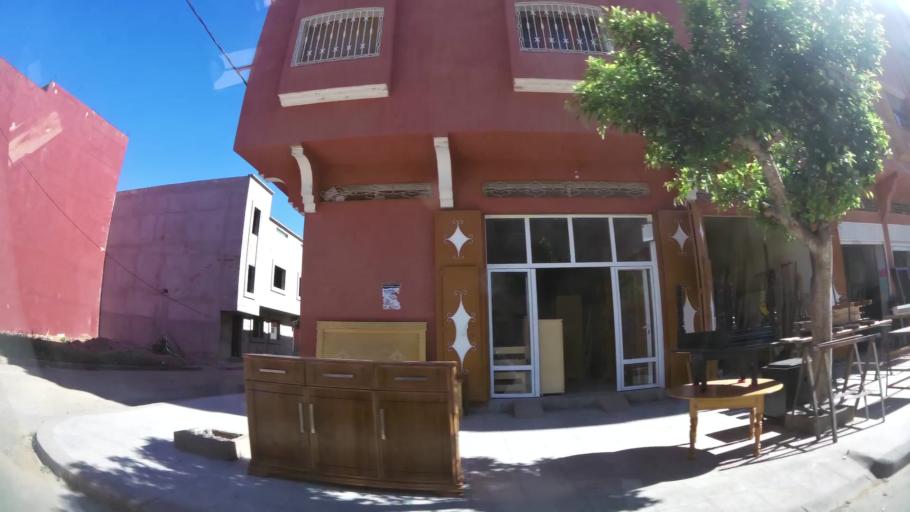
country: MA
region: Oriental
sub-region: Berkane-Taourirt
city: Berkane
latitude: 34.9388
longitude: -2.3355
